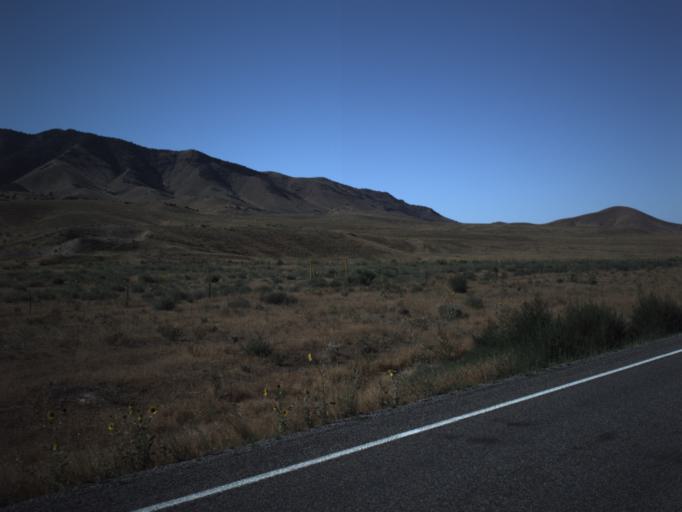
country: US
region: Utah
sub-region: Juab County
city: Nephi
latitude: 39.6721
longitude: -112.2644
